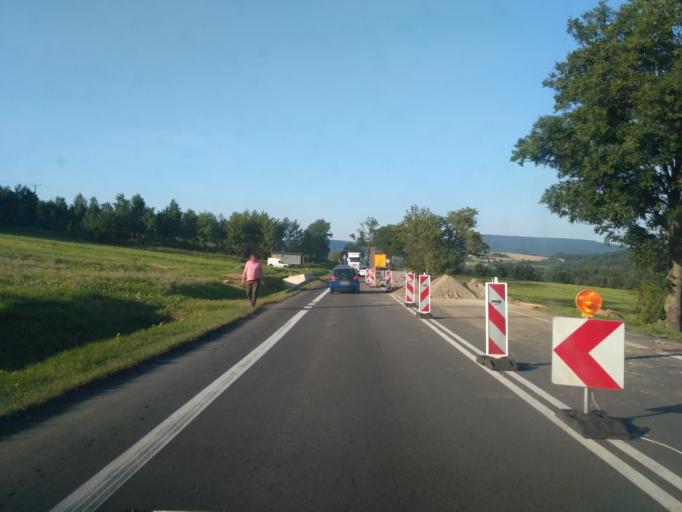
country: PL
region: Subcarpathian Voivodeship
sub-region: Powiat krosnienski
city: Dukla
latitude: 49.5859
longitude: 21.7058
